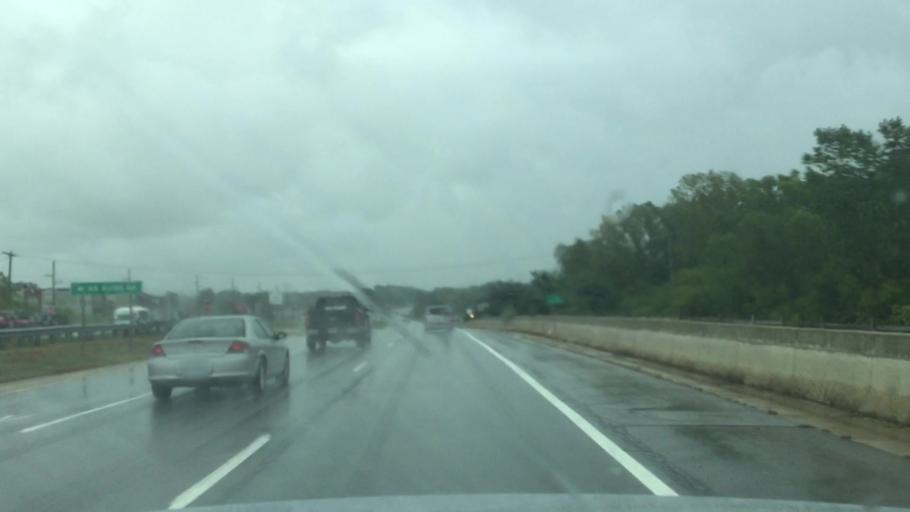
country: US
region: Michigan
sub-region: Livingston County
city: Howell
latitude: 42.6218
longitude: -83.9383
